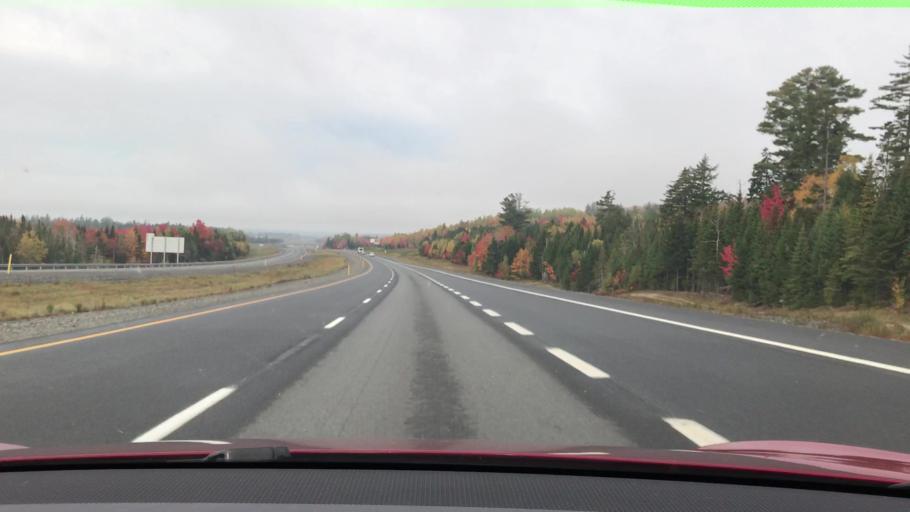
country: US
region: Maine
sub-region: Washington County
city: Calais
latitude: 45.2206
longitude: -67.2215
